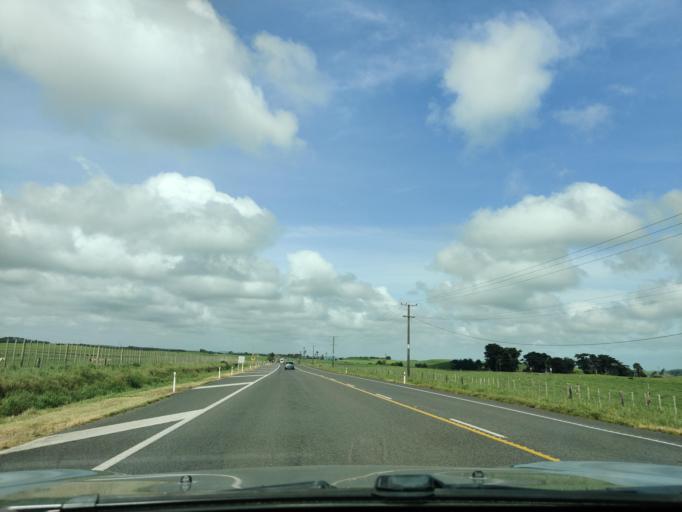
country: NZ
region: Taranaki
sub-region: South Taranaki District
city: Patea
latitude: -39.7688
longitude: 174.6584
